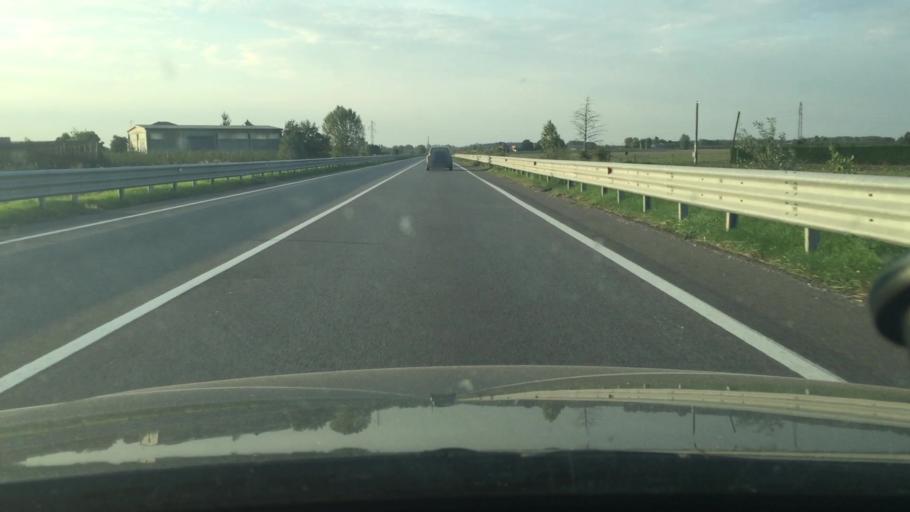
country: IT
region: Emilia-Romagna
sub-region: Provincia di Ferrara
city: Ferrara
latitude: 44.8304
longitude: 11.5798
